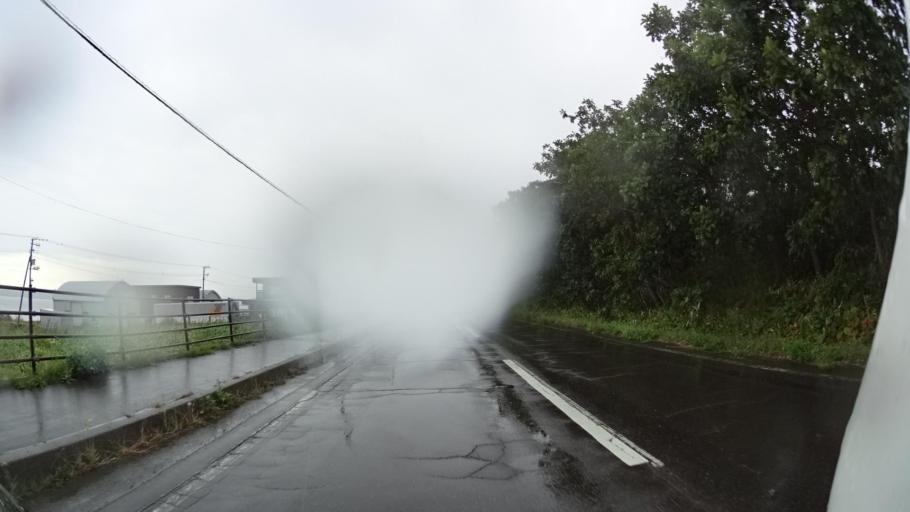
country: JP
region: Hokkaido
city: Mombetsu
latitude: 44.3327
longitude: 143.4896
